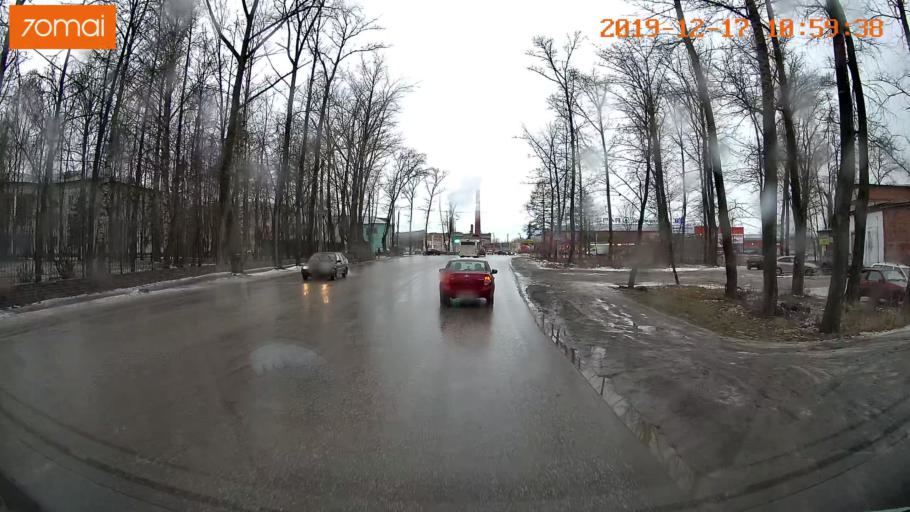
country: RU
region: Vladimir
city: Gus'-Khrustal'nyy
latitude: 55.6220
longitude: 40.6452
